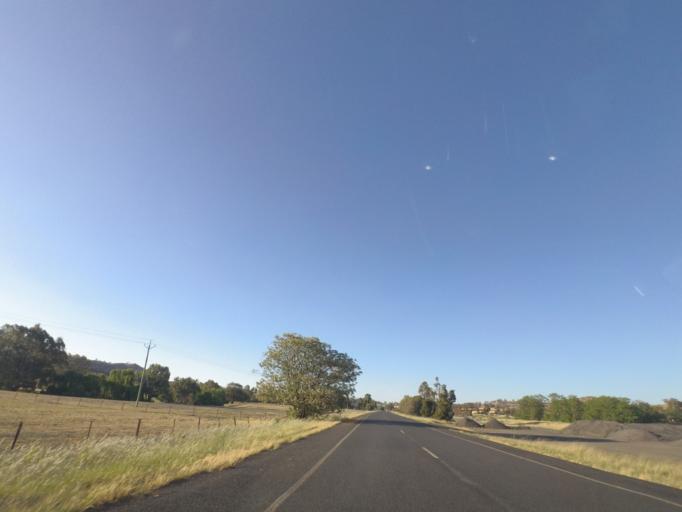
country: AU
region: New South Wales
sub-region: Gundagai
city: Gundagai
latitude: -34.9359
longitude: 148.1673
